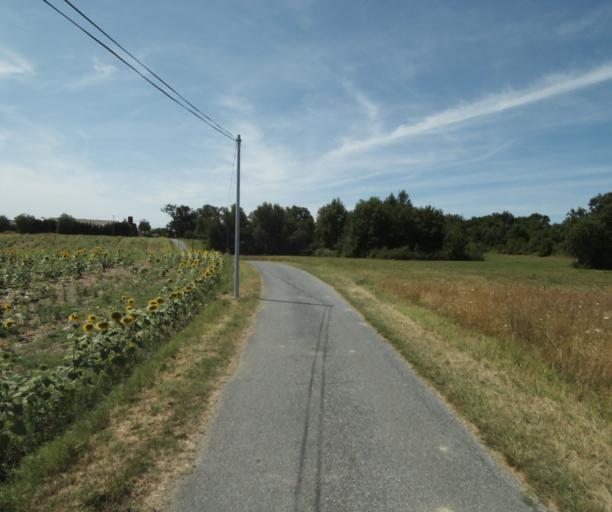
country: FR
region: Midi-Pyrenees
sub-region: Departement du Tarn
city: Puylaurens
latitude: 43.5351
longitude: 2.0020
